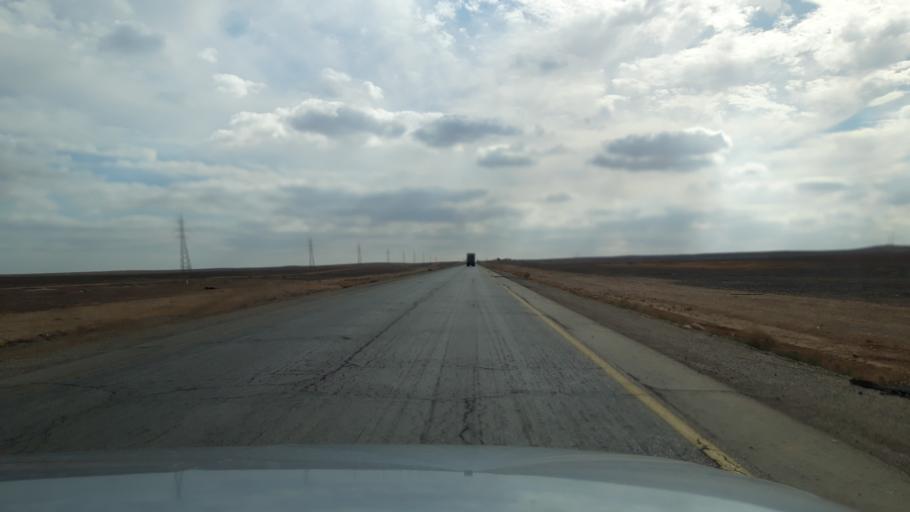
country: JO
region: Amman
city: Al Azraq ash Shamali
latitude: 31.7626
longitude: 36.5546
